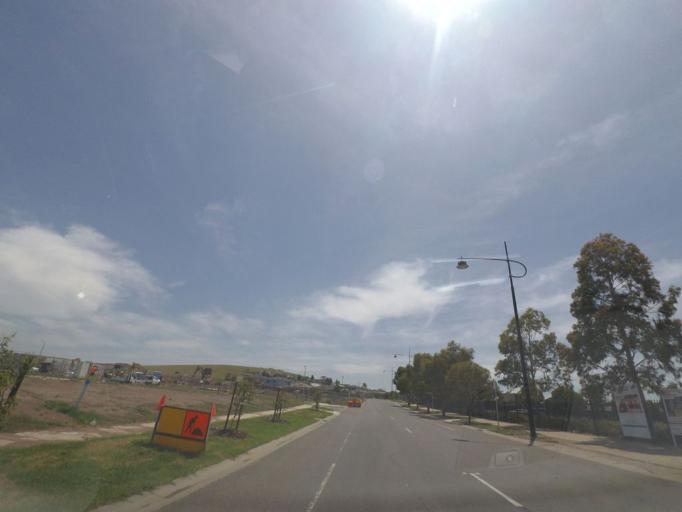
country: AU
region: Victoria
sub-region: Hume
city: Roxburgh Park
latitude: -37.6148
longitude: 144.9087
